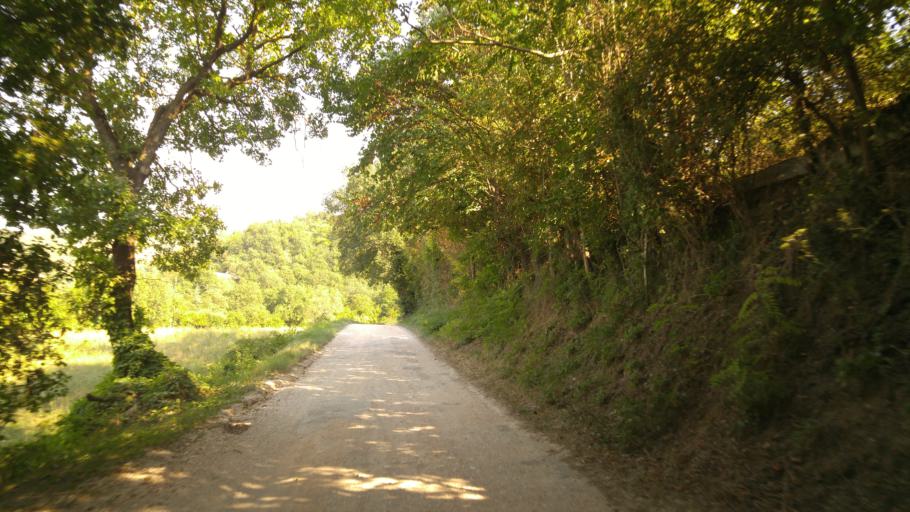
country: IT
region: The Marches
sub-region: Provincia di Pesaro e Urbino
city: Fossombrone
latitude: 43.6796
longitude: 12.7906
